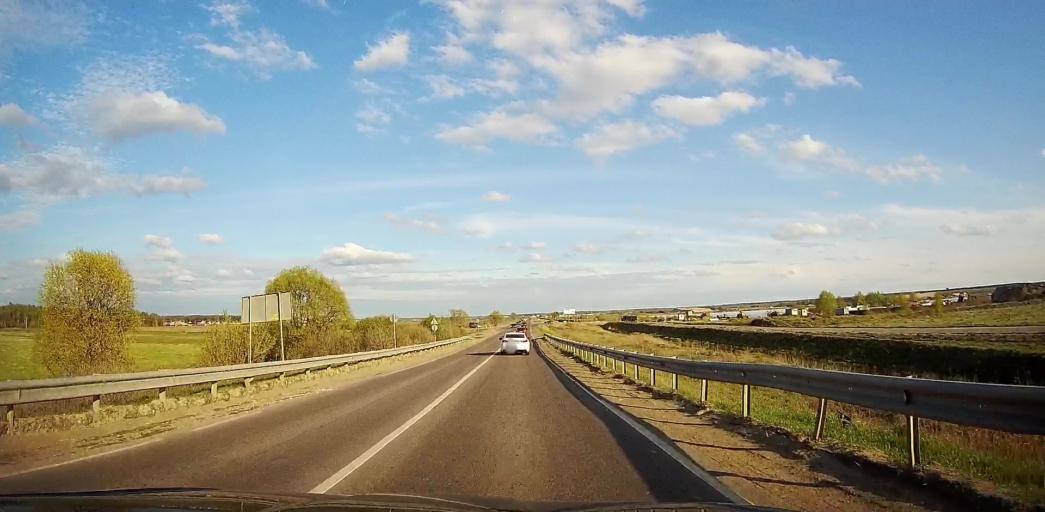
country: RU
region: Moskovskaya
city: Ramenskoye
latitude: 55.5137
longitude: 38.2768
